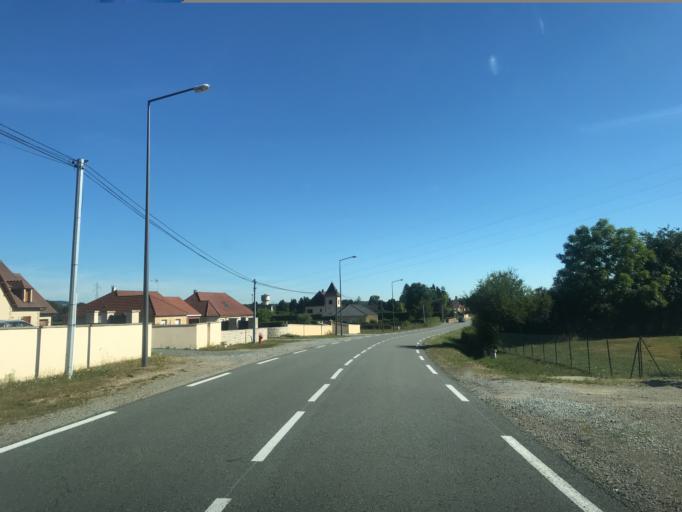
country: FR
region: Limousin
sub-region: Departement de la Creuse
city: Gouzon
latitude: 46.1836
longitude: 2.2311
